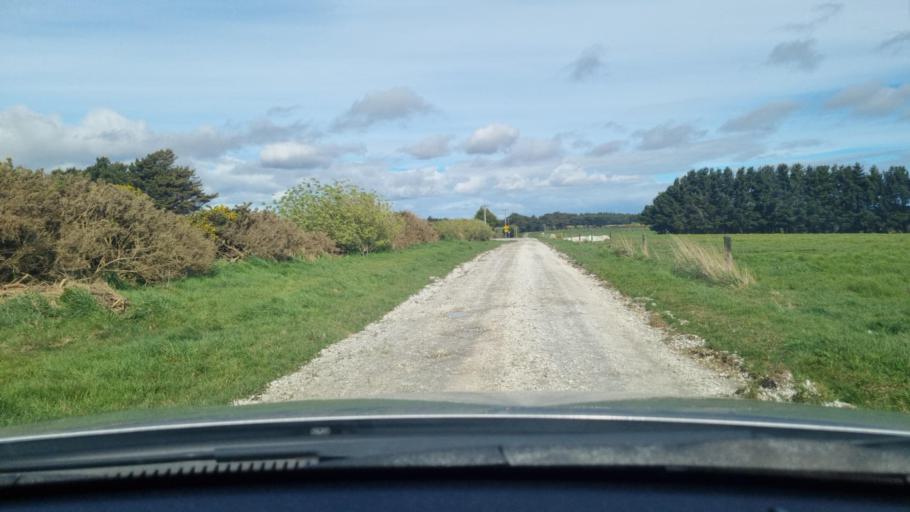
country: NZ
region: Southland
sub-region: Invercargill City
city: Invercargill
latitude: -46.4572
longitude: 168.3871
